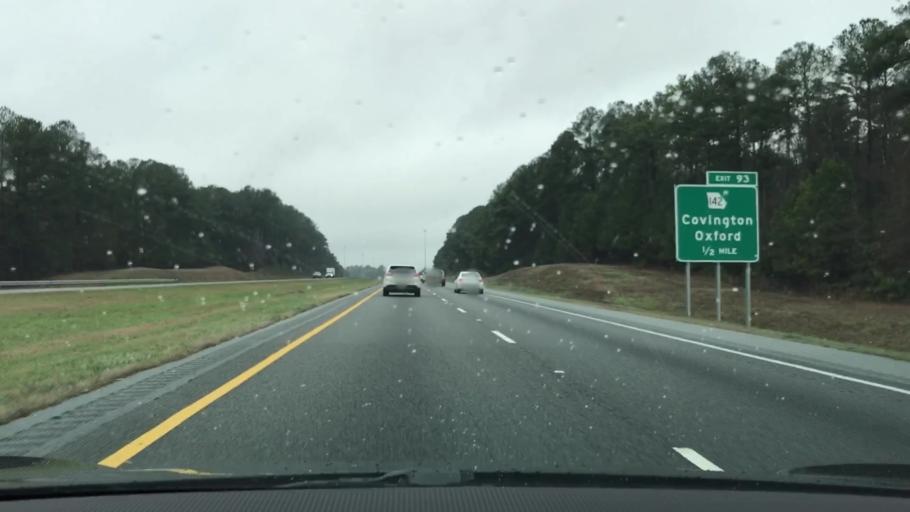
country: US
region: Georgia
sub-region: Newton County
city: Covington
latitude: 33.6115
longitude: -83.8122
